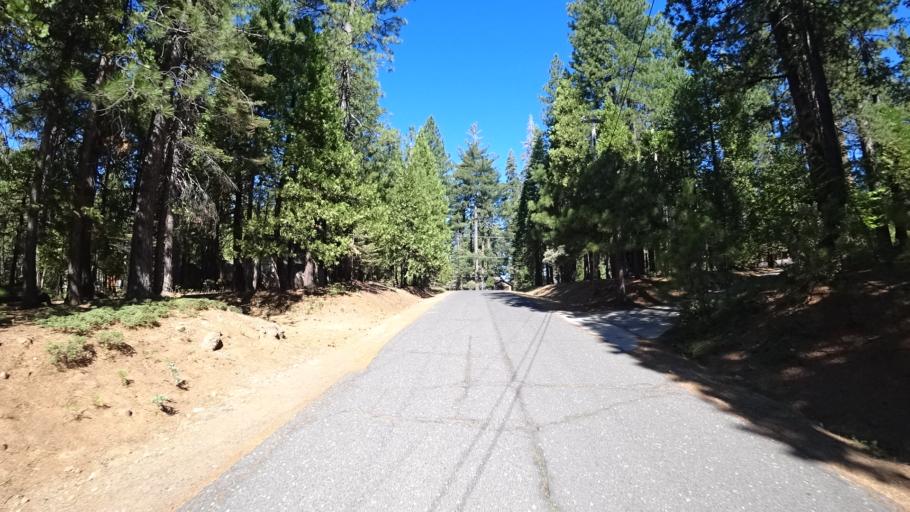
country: US
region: California
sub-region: Calaveras County
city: Arnold
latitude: 38.2460
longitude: -120.3264
